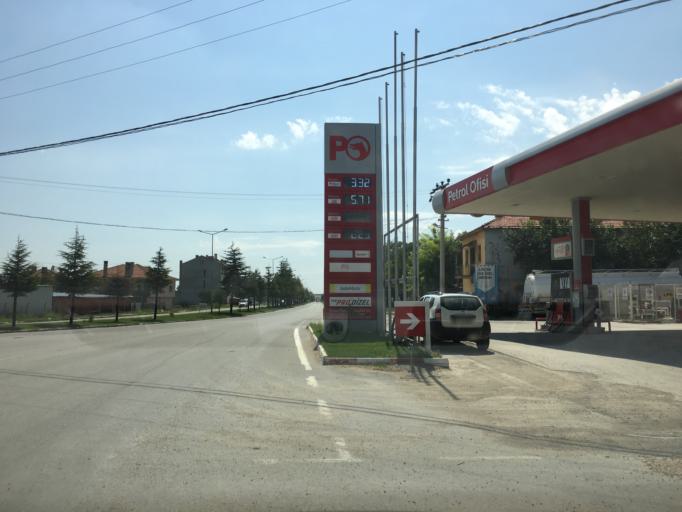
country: TR
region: Eskisehir
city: Cifteler
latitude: 39.3692
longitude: 31.0360
